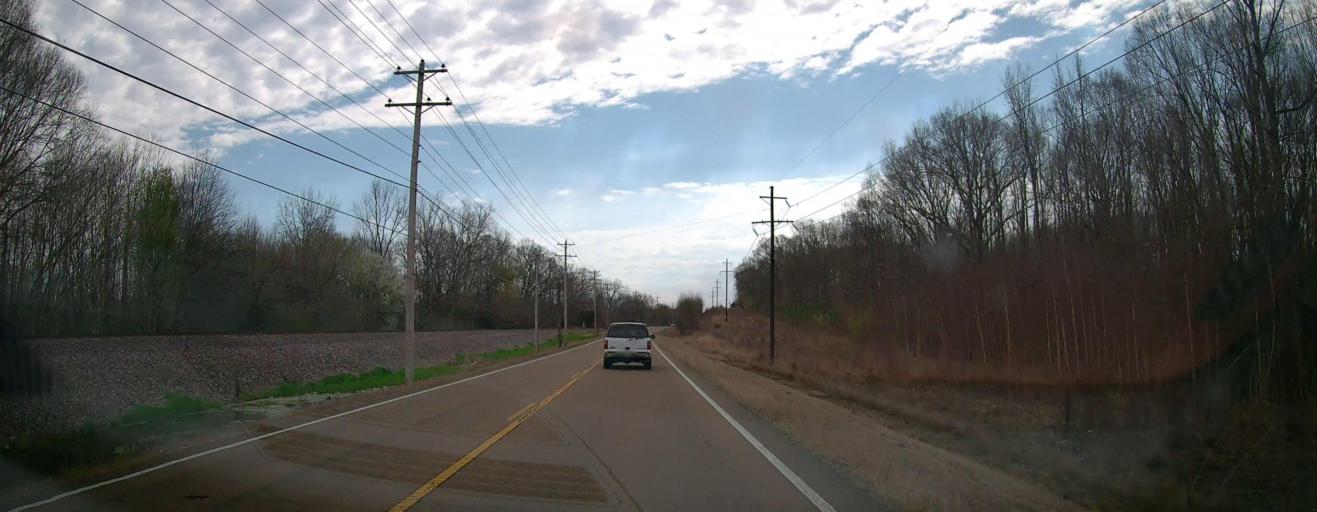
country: US
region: Mississippi
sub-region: Marshall County
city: Byhalia
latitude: 34.9031
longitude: -89.7466
